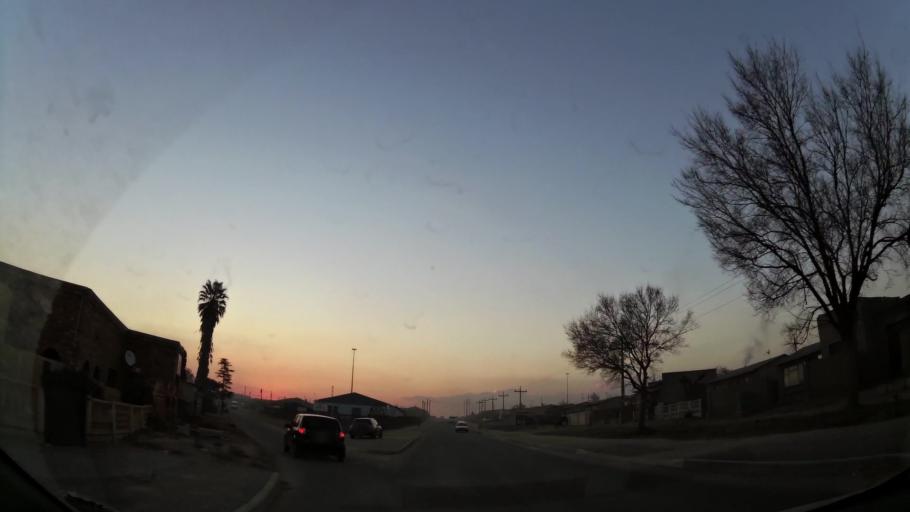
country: ZA
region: Gauteng
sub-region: Ekurhuleni Metropolitan Municipality
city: Nigel
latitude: -26.3728
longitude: 28.4013
